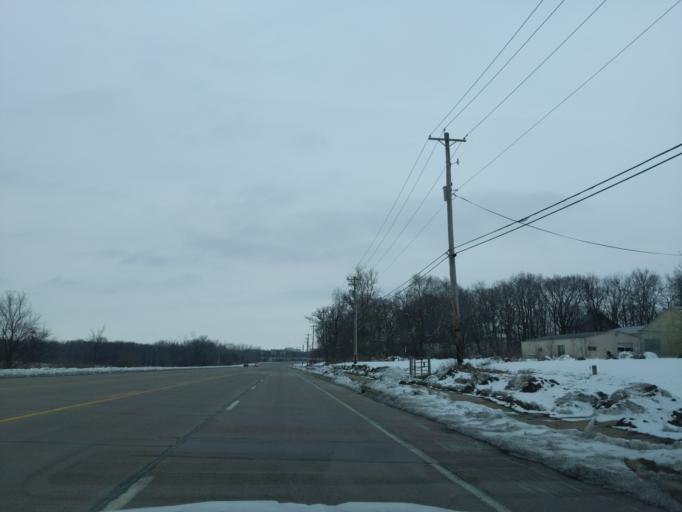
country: US
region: Indiana
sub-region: Tippecanoe County
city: West Lafayette
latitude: 40.4122
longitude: -86.9128
